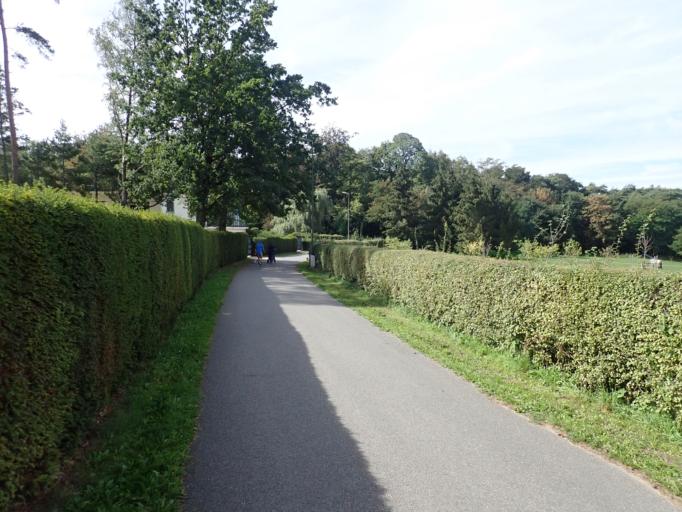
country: BE
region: Flanders
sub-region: Provincie Vlaams-Brabant
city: Oud-Heverlee
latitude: 50.8317
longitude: 4.6552
